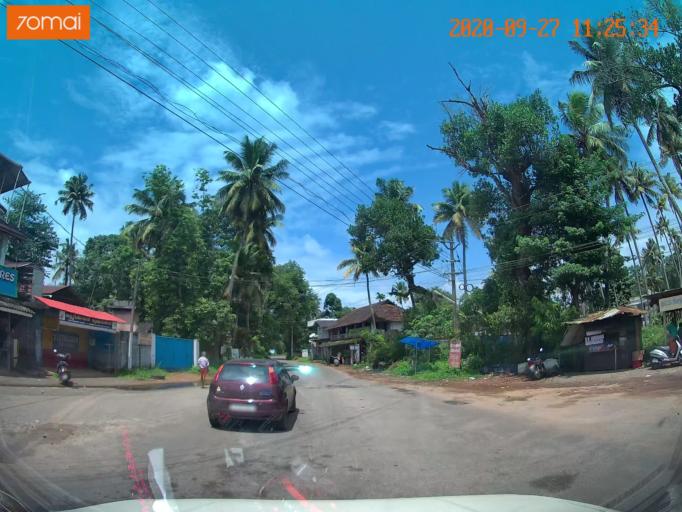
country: IN
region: Kerala
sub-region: Thrissur District
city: Thanniyam
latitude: 10.4141
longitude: 76.1574
